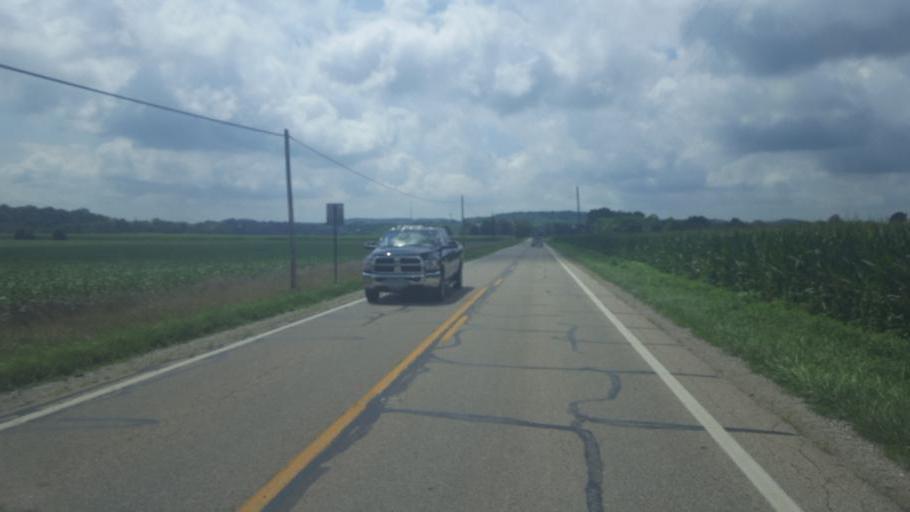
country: US
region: Ohio
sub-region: Ross County
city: Kingston
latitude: 39.4874
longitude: -82.7567
